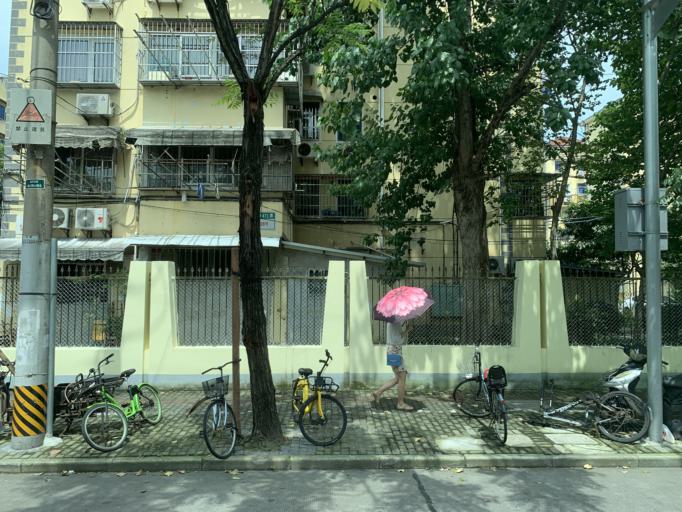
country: CN
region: Shanghai Shi
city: Huamu
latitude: 31.2476
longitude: 121.5768
